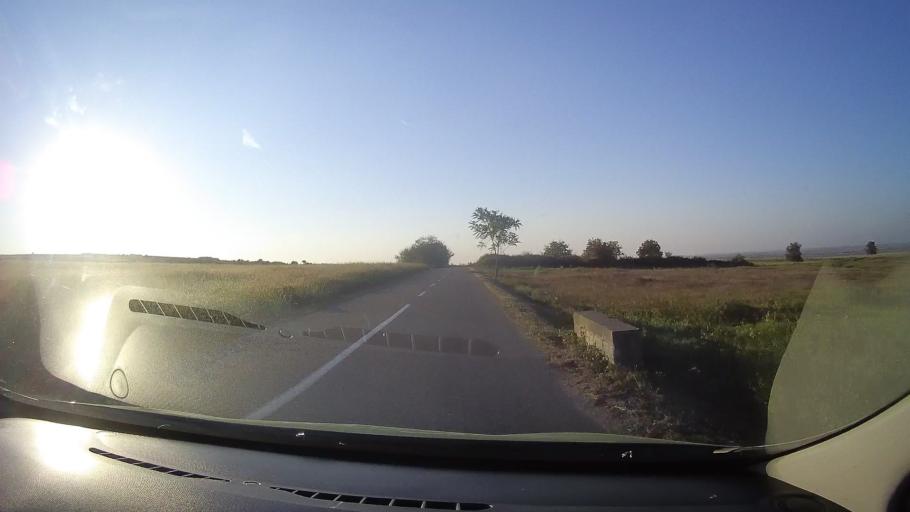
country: RO
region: Bihor
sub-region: Comuna Cetariu
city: Cetariu
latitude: 47.1531
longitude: 21.9901
